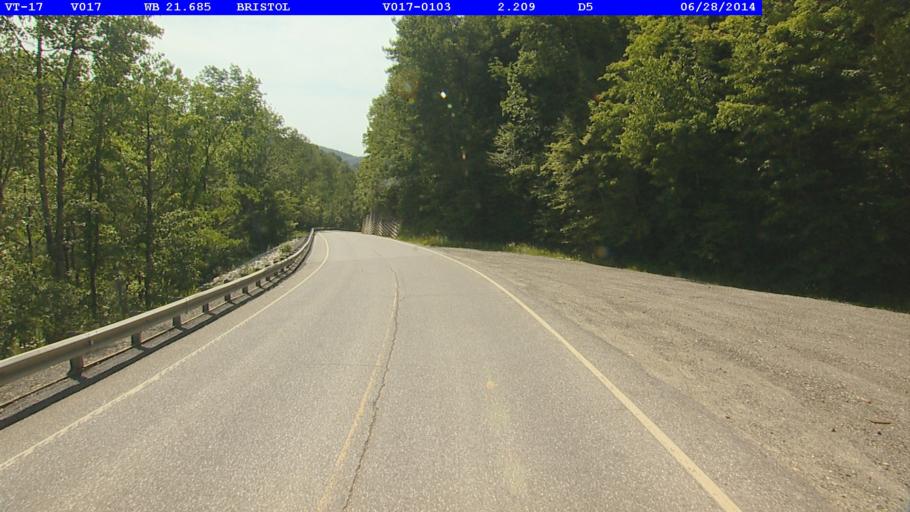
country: US
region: Vermont
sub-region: Addison County
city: Bristol
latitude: 44.1623
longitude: -73.0194
